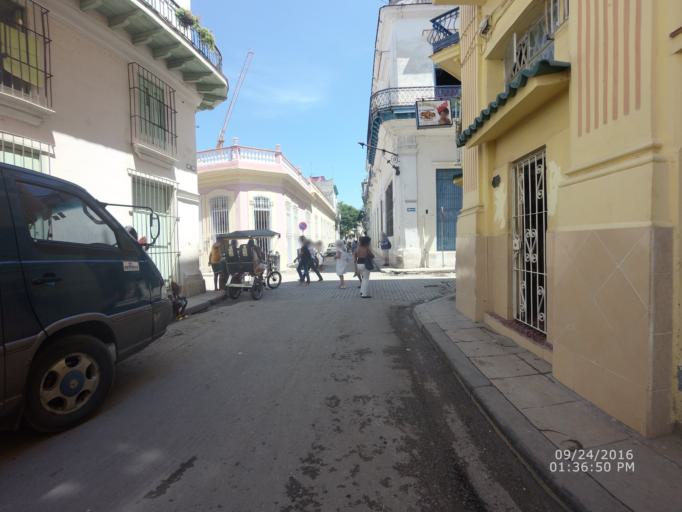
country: CU
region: La Habana
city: La Habana Vieja
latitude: 23.1347
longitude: -82.3505
